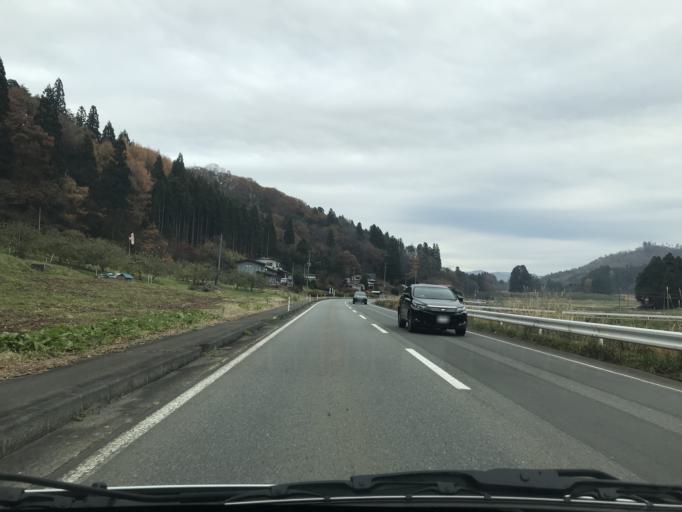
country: JP
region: Iwate
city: Kitakami
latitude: 39.2957
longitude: 141.1840
